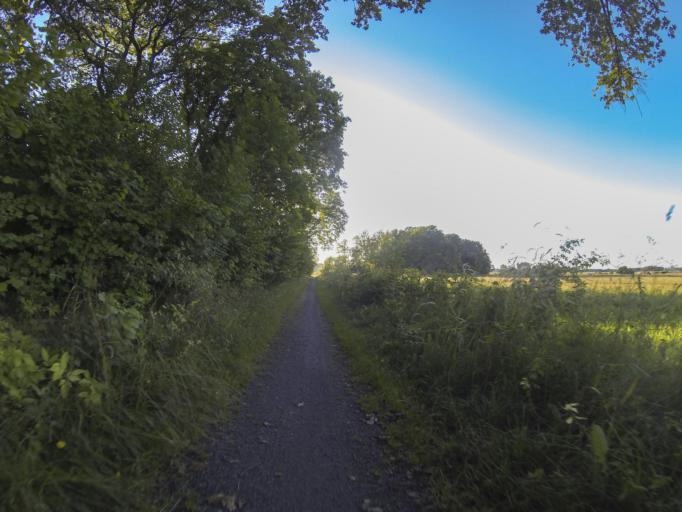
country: SE
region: Vaestmanland
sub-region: Vasteras
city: Vasteras
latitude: 59.5567
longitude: 16.6495
